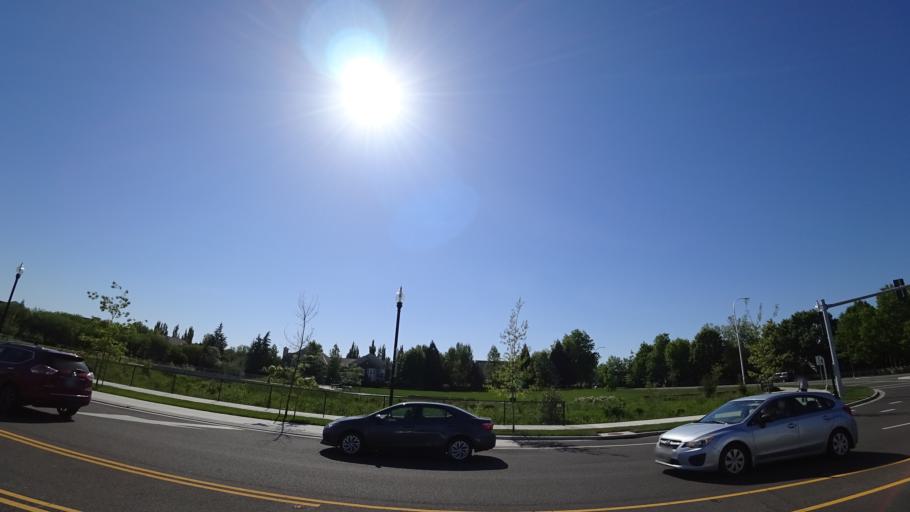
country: US
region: Oregon
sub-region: Washington County
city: Rockcreek
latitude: 45.5337
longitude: -122.9119
